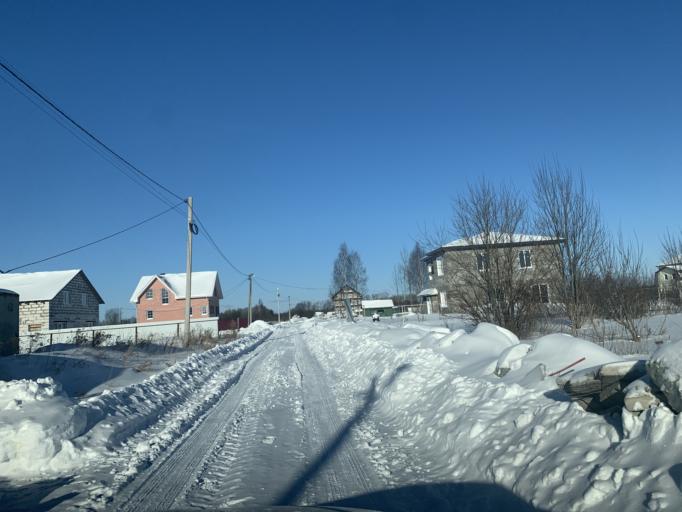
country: RU
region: Jaroslavl
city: Tunoshna
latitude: 57.6641
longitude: 40.0667
